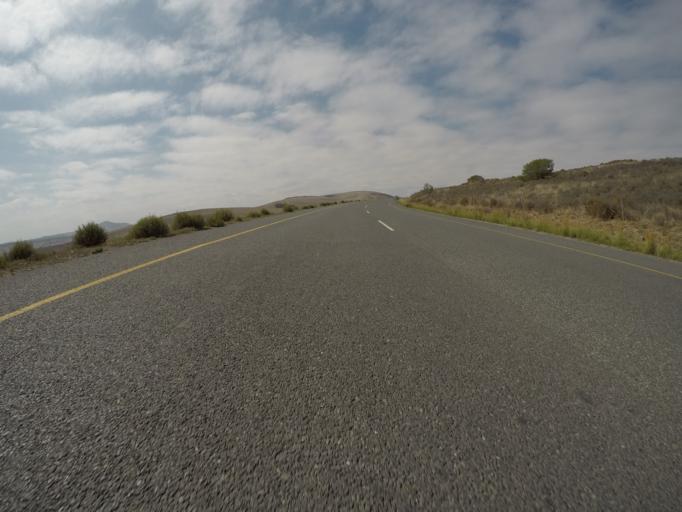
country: ZA
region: Western Cape
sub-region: City of Cape Town
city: Sunset Beach
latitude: -33.7901
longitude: 18.5718
